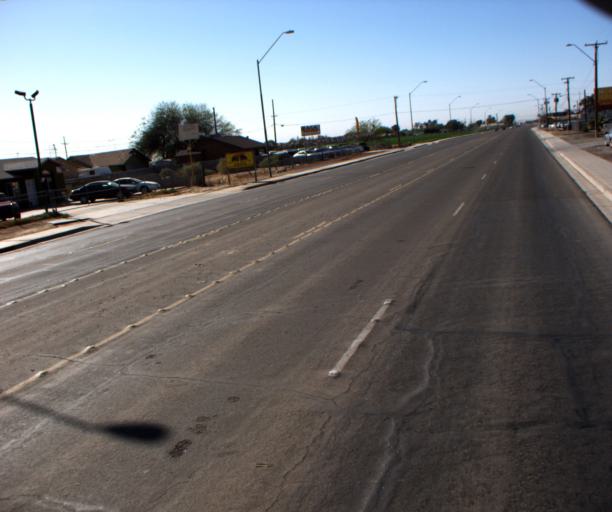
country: US
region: Arizona
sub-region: Yuma County
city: San Luis
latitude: 32.5611
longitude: -114.7848
